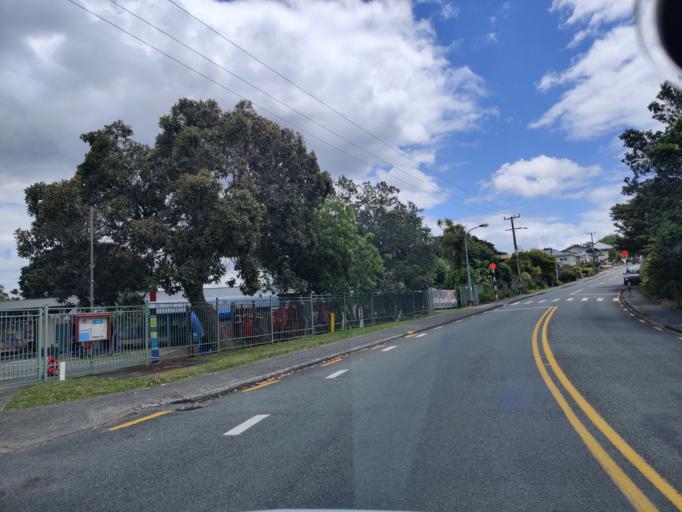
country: NZ
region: Northland
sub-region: Far North District
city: Paihia
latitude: -35.3144
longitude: 174.1182
